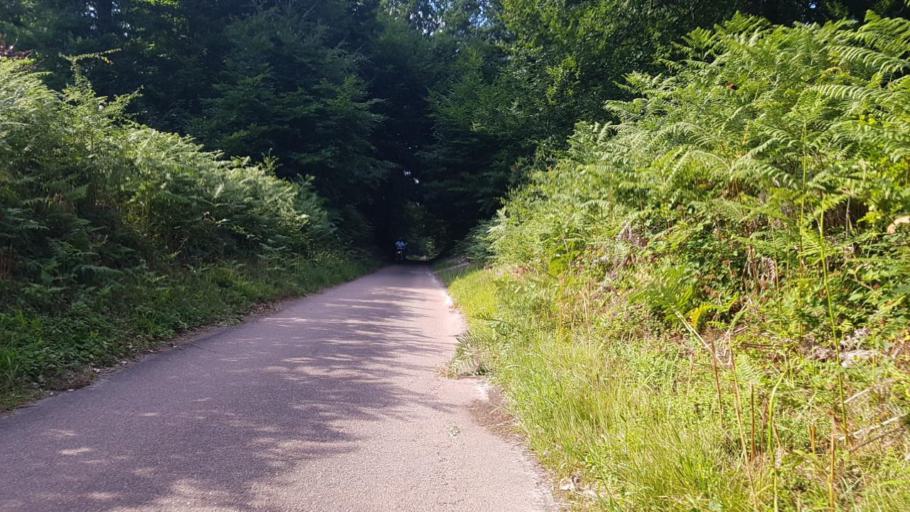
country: FR
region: Picardie
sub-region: Departement de l'Oise
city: Thiers-sur-Theve
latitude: 49.1568
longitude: 2.6372
